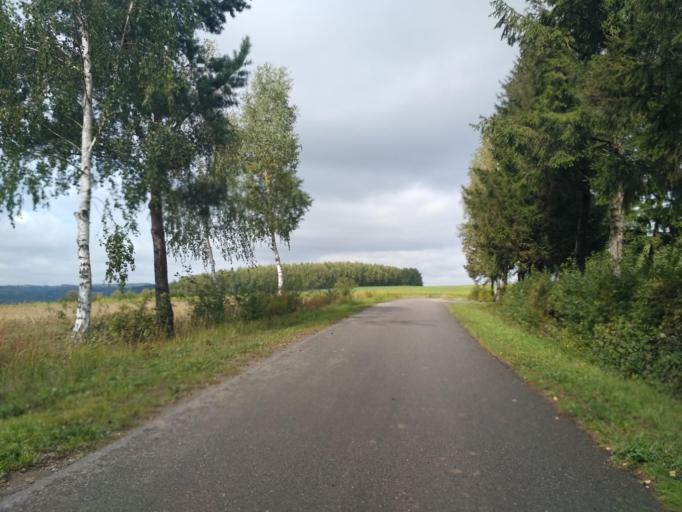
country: PL
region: Subcarpathian Voivodeship
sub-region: Powiat ropczycko-sedziszowski
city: Niedzwiada
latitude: 49.9298
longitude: 21.5035
